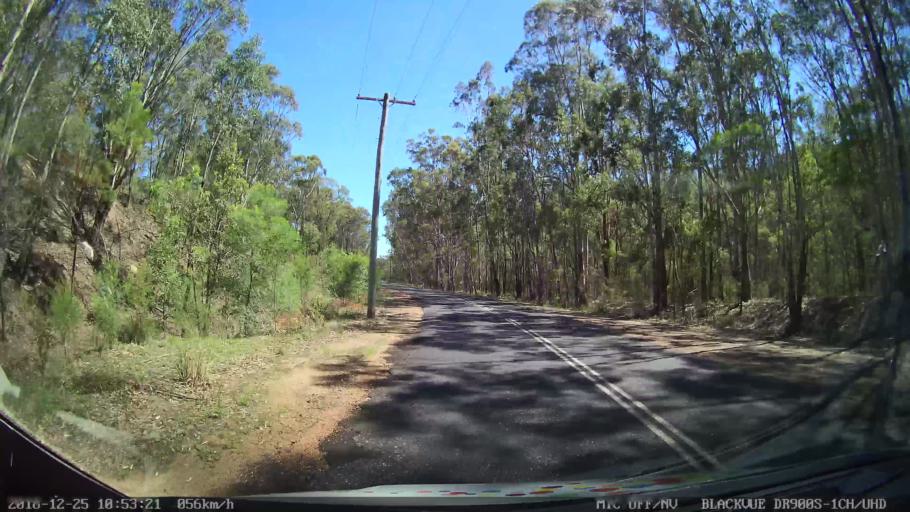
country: AU
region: New South Wales
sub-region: Upper Hunter Shire
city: Merriwa
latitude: -32.4209
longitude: 150.2734
